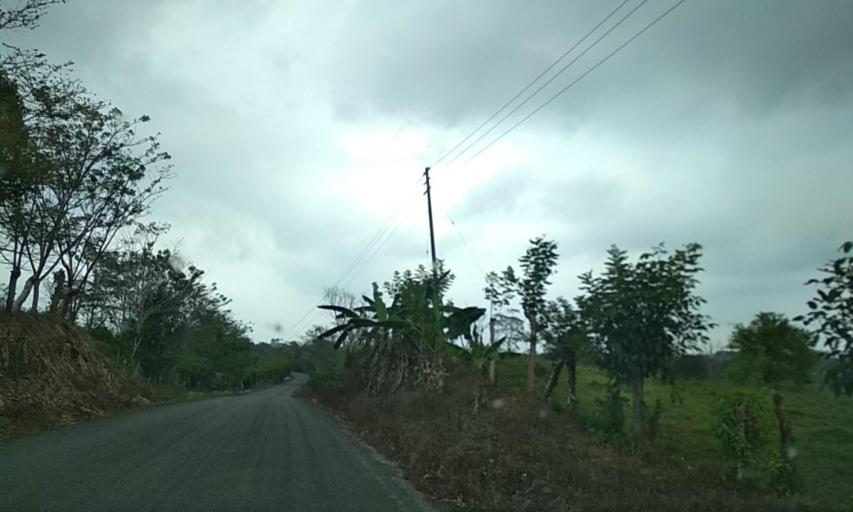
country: MX
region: Tabasco
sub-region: Huimanguillo
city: Francisco Rueda
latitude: 17.5752
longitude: -94.1035
